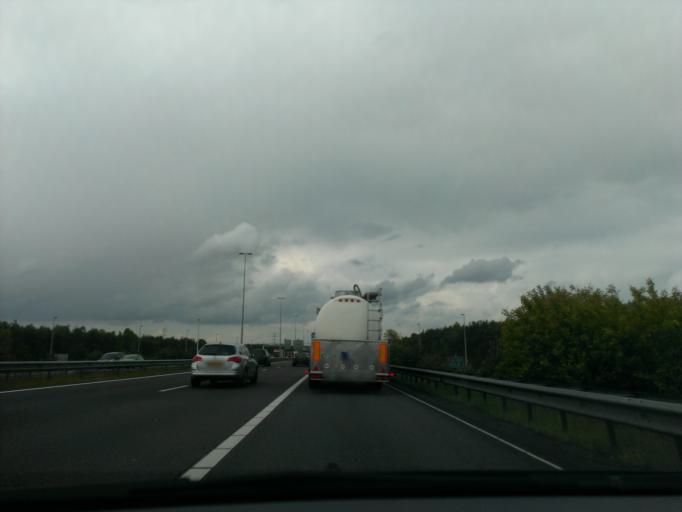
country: NL
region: Gelderland
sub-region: Gemeente Rozendaal
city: Rozendaal
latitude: 52.0252
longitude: 5.9252
